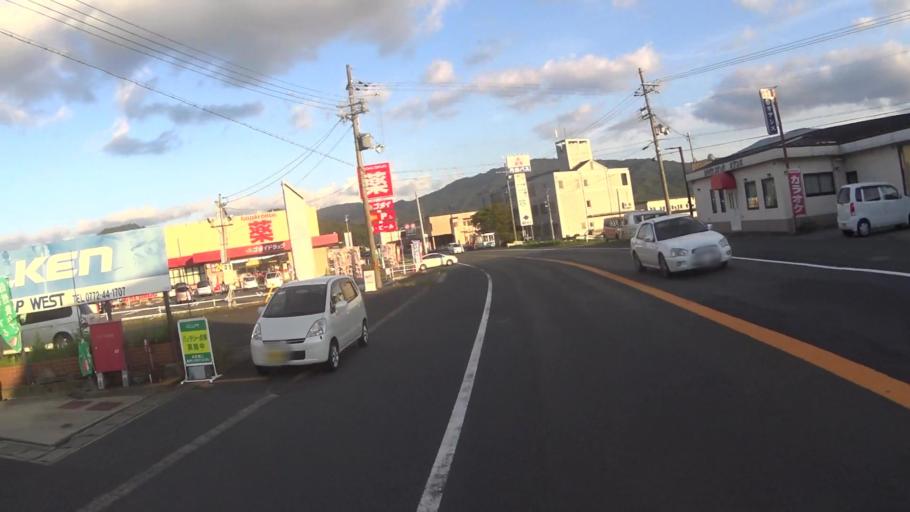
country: JP
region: Kyoto
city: Miyazu
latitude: 35.5363
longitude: 135.1144
